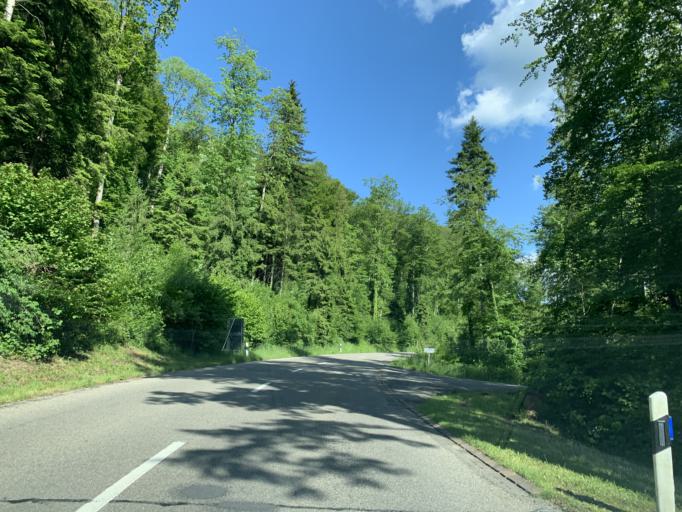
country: CH
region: Zurich
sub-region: Bezirk Pfaeffikon
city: Effretikon / Watt
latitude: 47.4418
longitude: 8.7075
